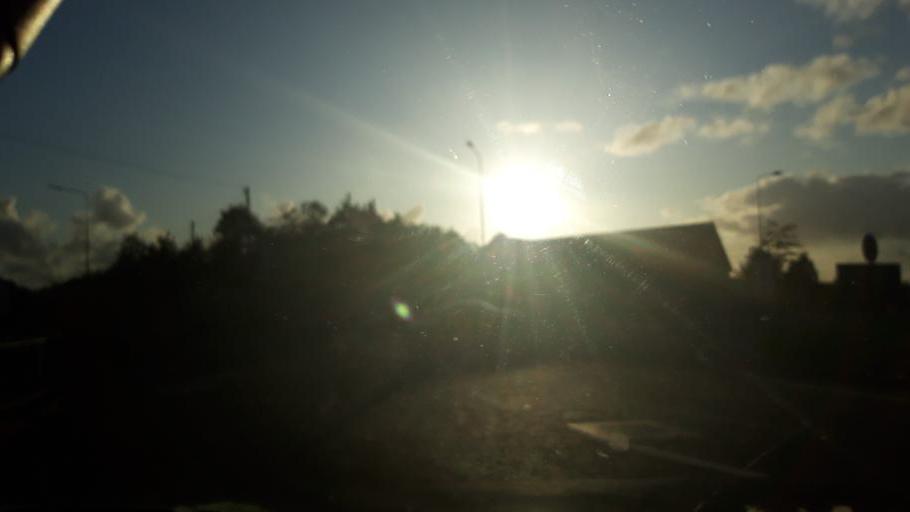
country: IE
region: Leinster
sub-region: An Iarmhi
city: Athlone
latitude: 53.4357
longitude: -7.9025
